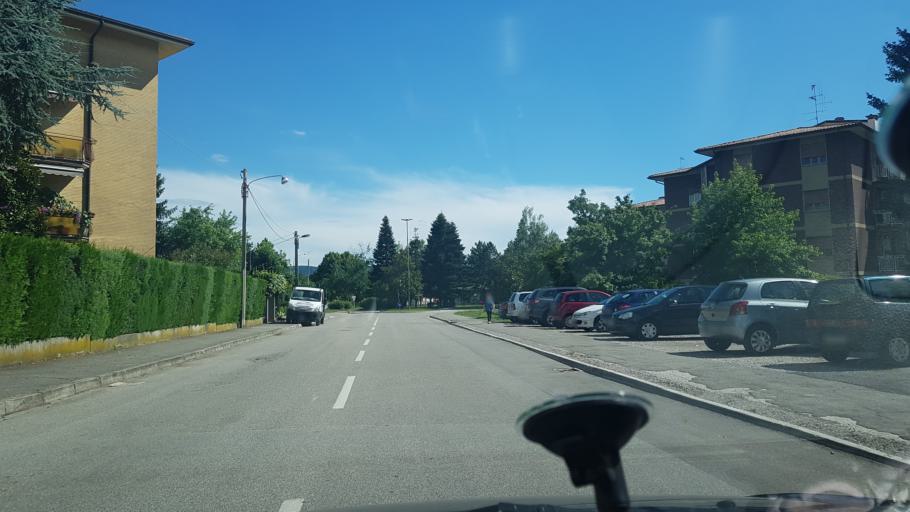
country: IT
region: Friuli Venezia Giulia
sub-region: Provincia di Gorizia
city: Gorizia
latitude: 45.9314
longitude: 13.6217
